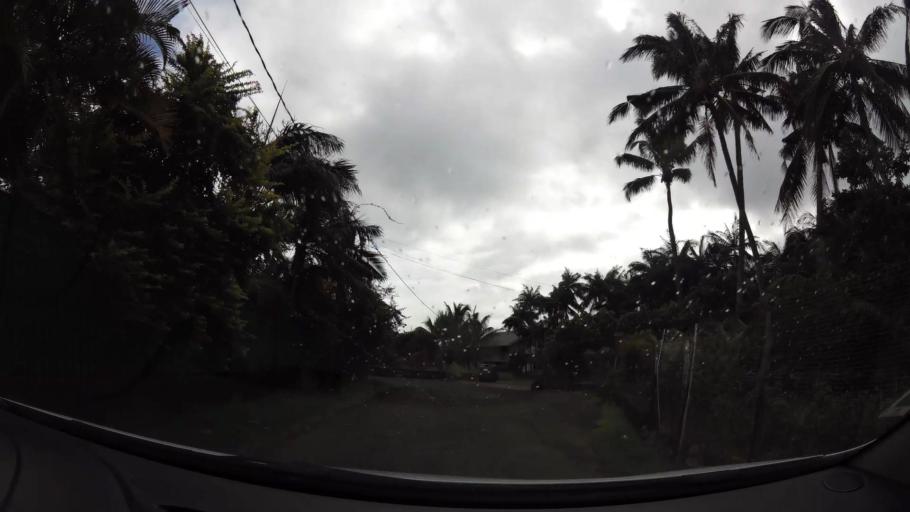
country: RE
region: Reunion
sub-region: Reunion
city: Sainte-Suzanne
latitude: -20.8997
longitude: 55.5988
